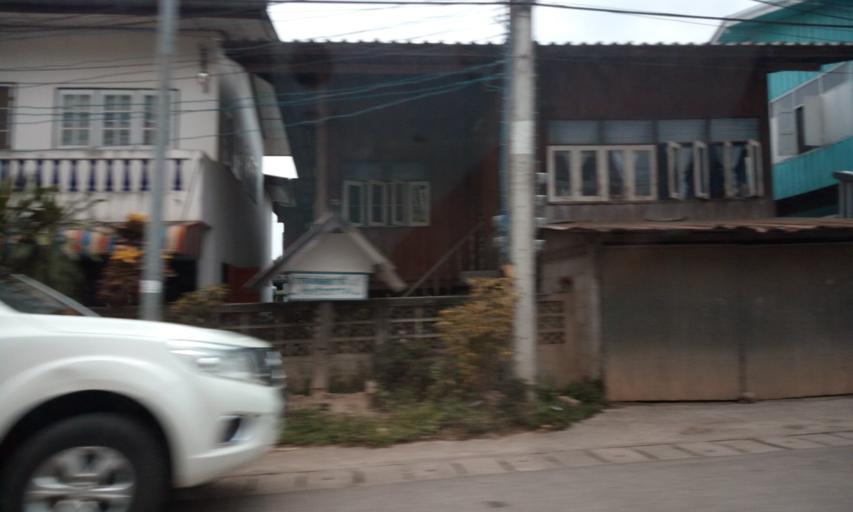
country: TH
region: Phayao
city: Chiang Kham
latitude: 19.5202
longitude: 100.3091
